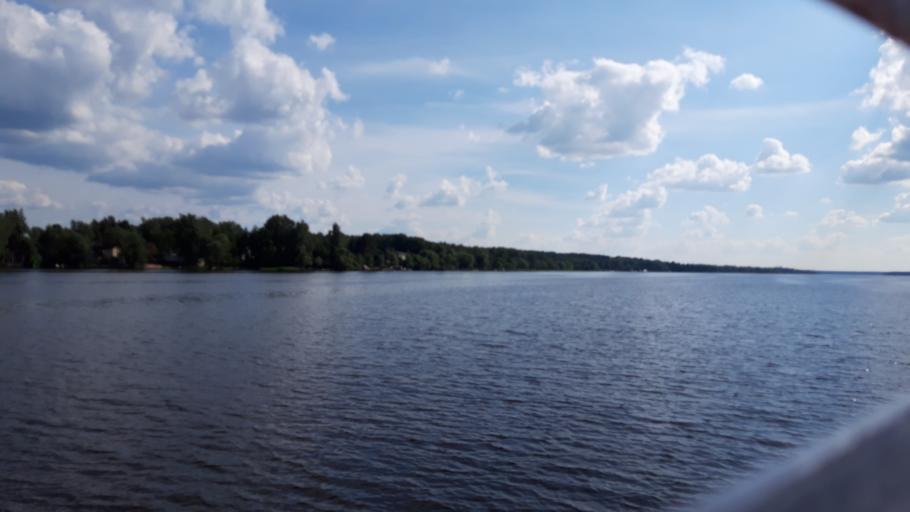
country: RU
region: Tverskaya
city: Konakovo
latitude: 56.6640
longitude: 36.6527
